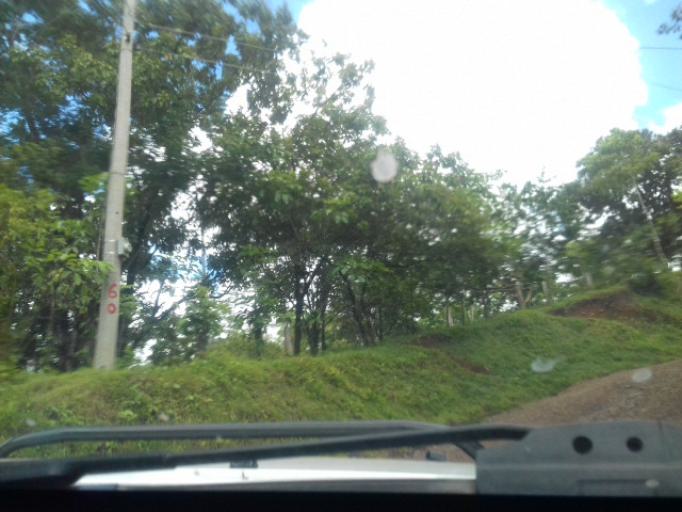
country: NI
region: Matagalpa
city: Rio Blanco
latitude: 13.0040
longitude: -85.2014
